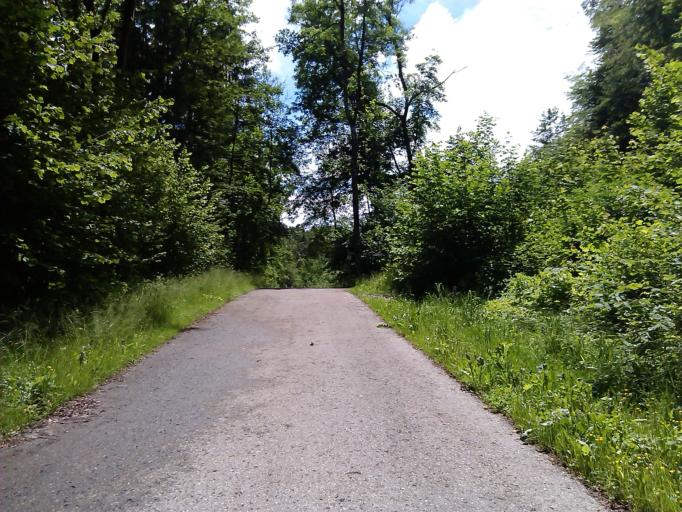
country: DE
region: Bavaria
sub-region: Swabia
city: Biessenhofen
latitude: 47.8537
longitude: 10.6323
